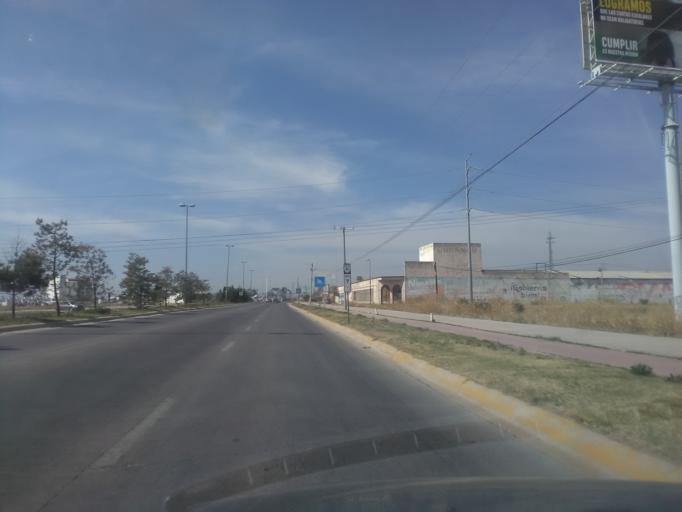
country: MX
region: Durango
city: Victoria de Durango
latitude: 24.0776
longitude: -104.5905
